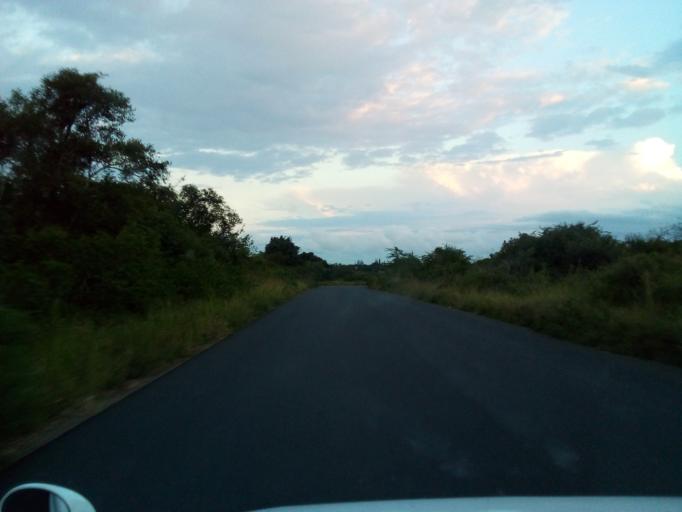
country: MZ
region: Maputo City
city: Maputo
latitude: -26.3332
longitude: 32.6647
